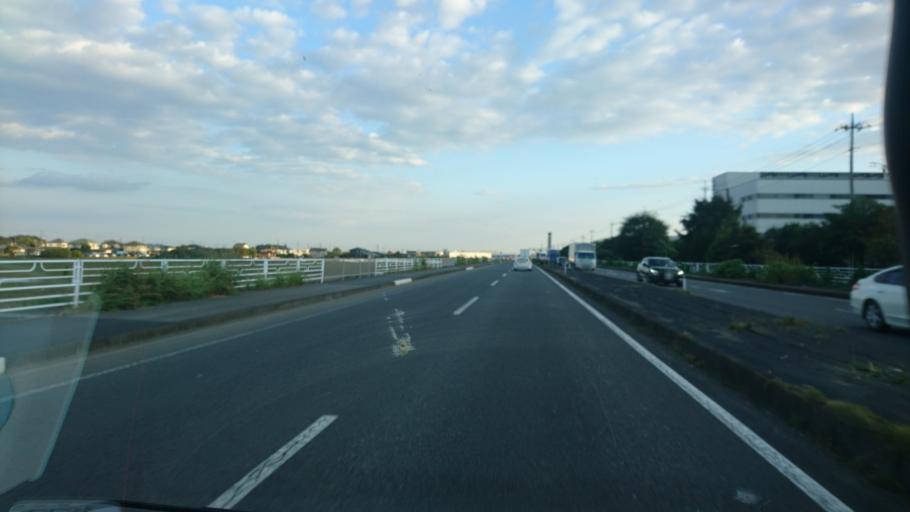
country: JP
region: Gunma
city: Ota
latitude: 36.3564
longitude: 139.3736
